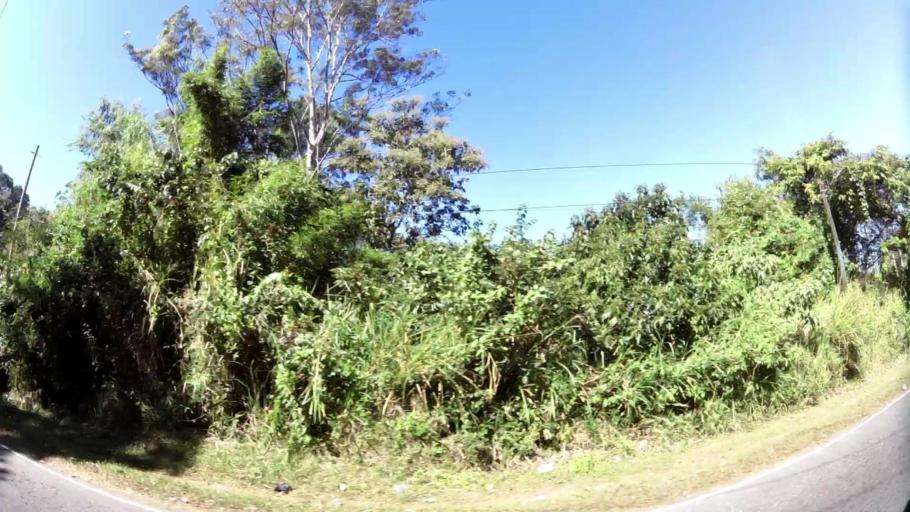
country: SV
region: Ahuachapan
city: Concepcion de Ataco
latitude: 13.8878
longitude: -89.8411
